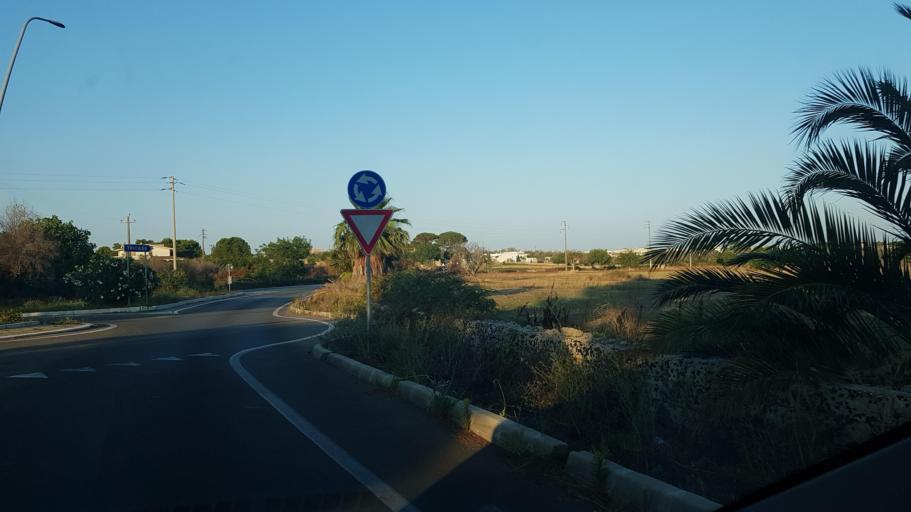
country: IT
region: Apulia
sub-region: Provincia di Lecce
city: Specchia
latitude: 39.9385
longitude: 18.3073
